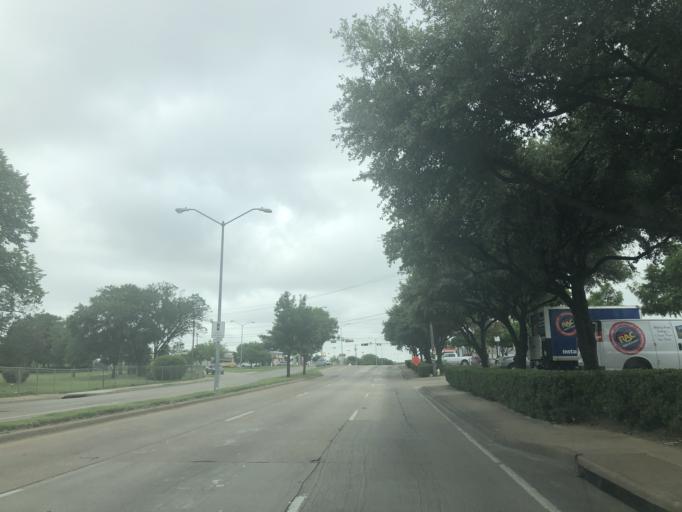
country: US
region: Texas
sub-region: Dallas County
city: Farmers Branch
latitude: 32.8679
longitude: -96.8649
